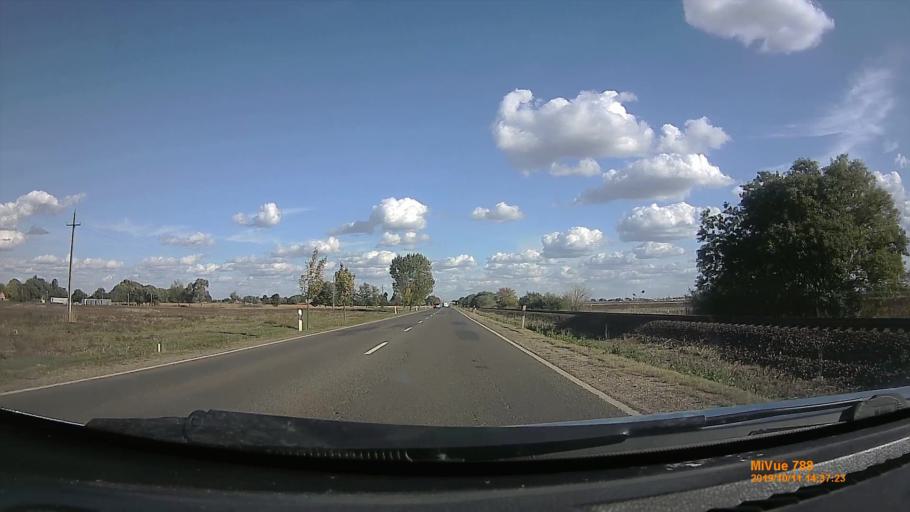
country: HU
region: Hajdu-Bihar
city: Ebes
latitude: 47.5541
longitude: 21.5251
